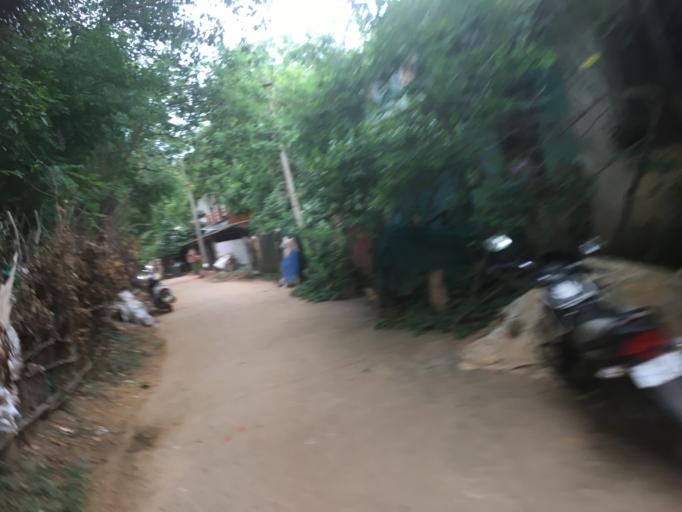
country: IN
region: Tamil Nadu
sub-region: Villupuram
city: Auroville
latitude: 12.0094
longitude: 79.8020
